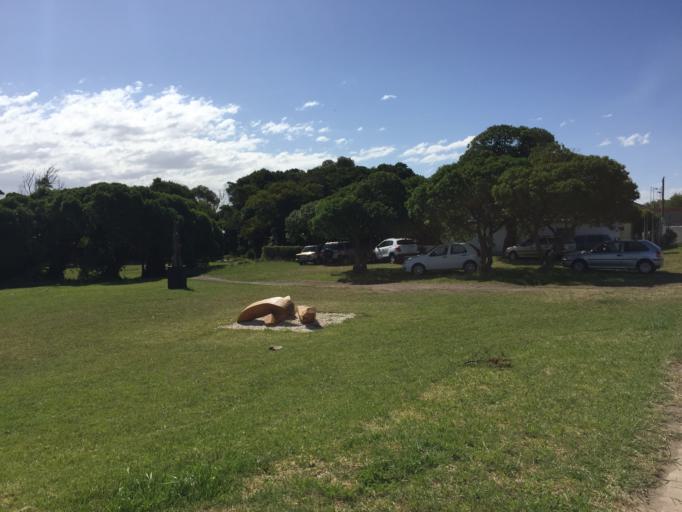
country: AR
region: Buenos Aires
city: Miramar
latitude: -38.2676
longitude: -57.8278
